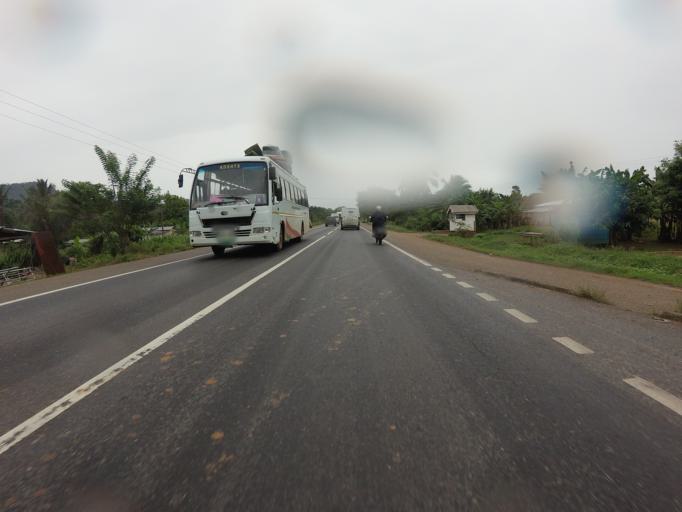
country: GH
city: Kibi
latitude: 6.1311
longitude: -0.4949
